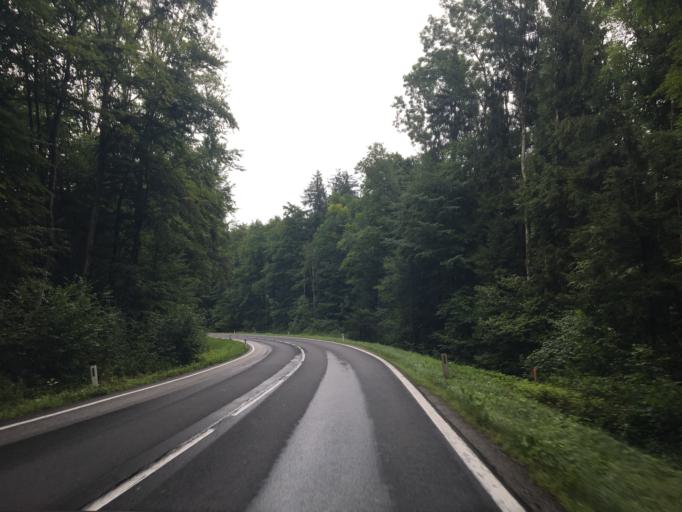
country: AT
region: Salzburg
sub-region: Politischer Bezirk Salzburg-Umgebung
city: Dorfbeuern
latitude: 48.1174
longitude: 13.0040
